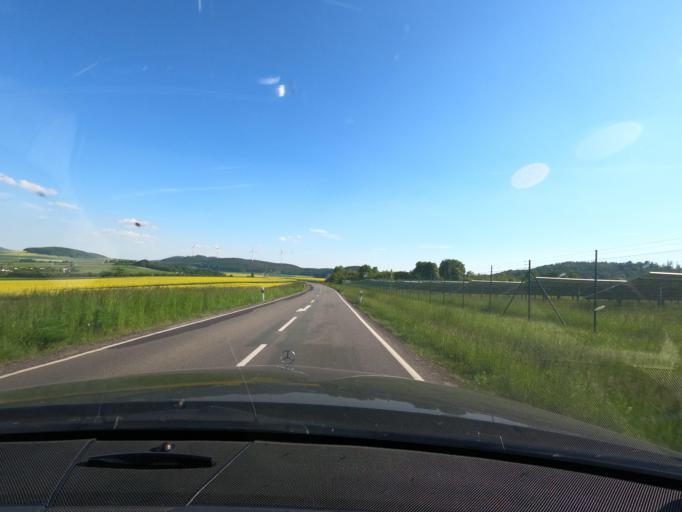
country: DE
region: Hesse
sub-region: Regierungsbezirk Kassel
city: Breuna
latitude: 51.3970
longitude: 9.1839
